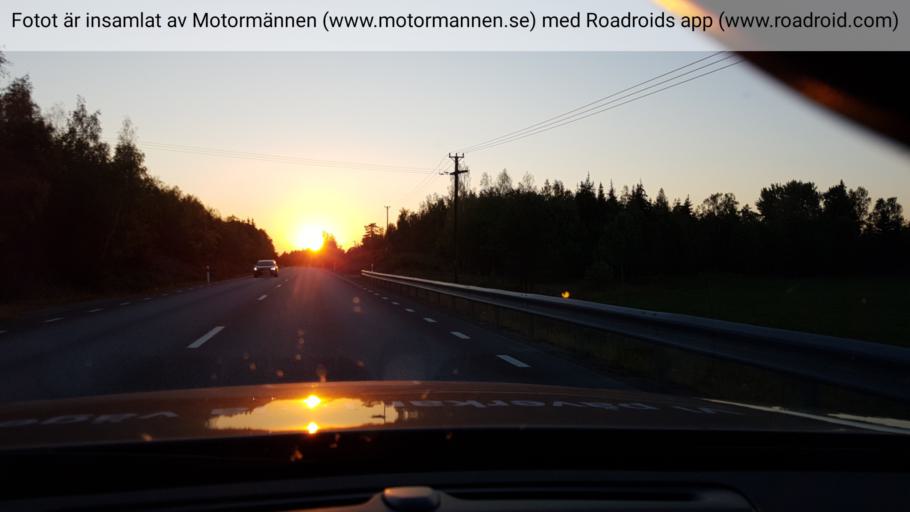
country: SE
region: Uppsala
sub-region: Osthammars Kommun
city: Bjorklinge
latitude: 59.9735
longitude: 17.3606
